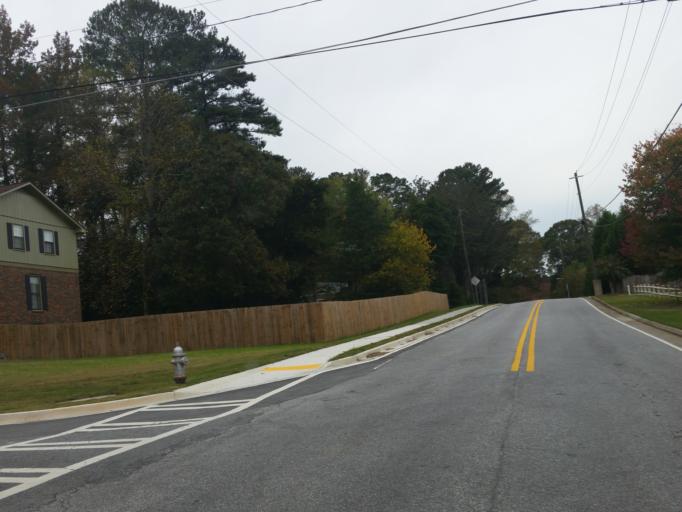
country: US
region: Georgia
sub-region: Cobb County
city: Marietta
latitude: 33.9525
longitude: -84.4713
